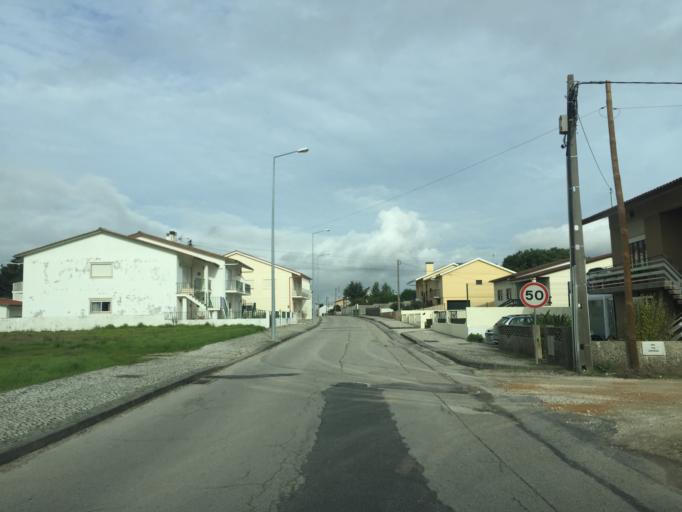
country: PT
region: Coimbra
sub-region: Figueira da Foz
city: Lavos
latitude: 40.0645
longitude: -8.8100
